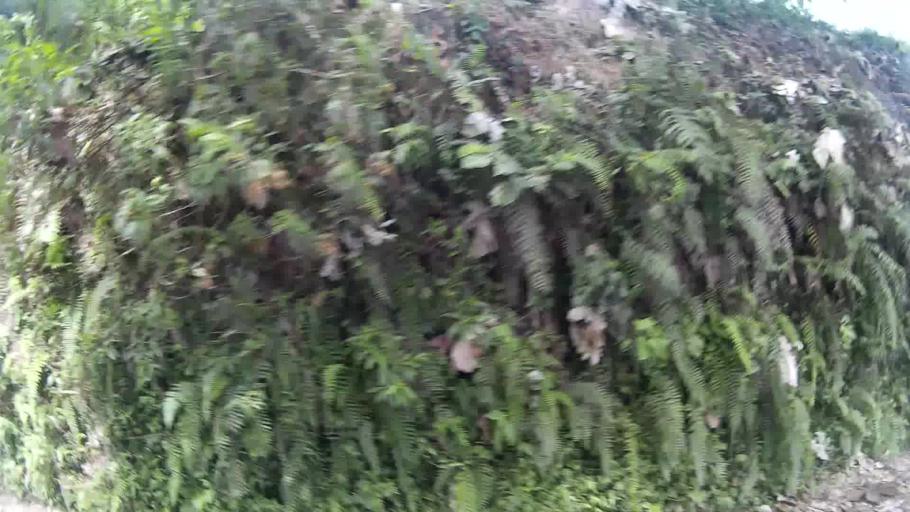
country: CO
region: Quindio
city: Filandia
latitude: 4.7146
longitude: -75.6564
